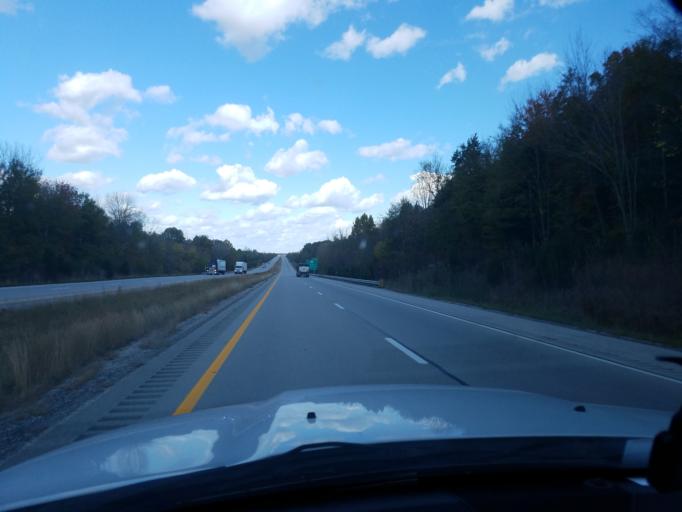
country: US
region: Kentucky
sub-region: Ohio County
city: Oak Grove
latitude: 37.2693
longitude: -86.7475
